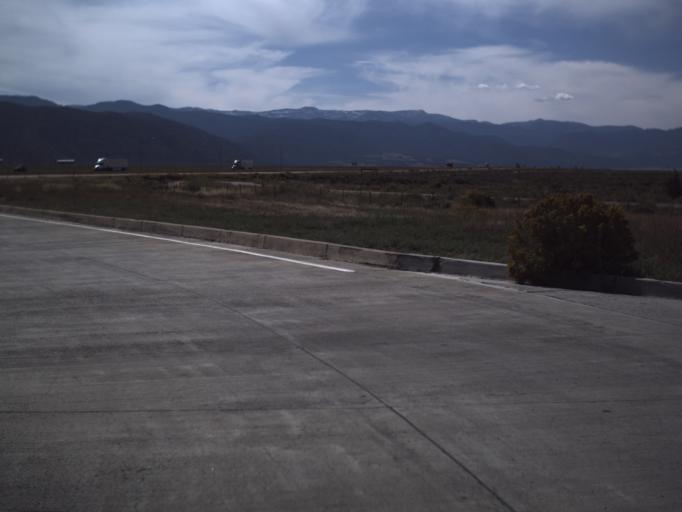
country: US
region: Utah
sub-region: Iron County
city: Parowan
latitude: 37.9819
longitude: -112.7389
